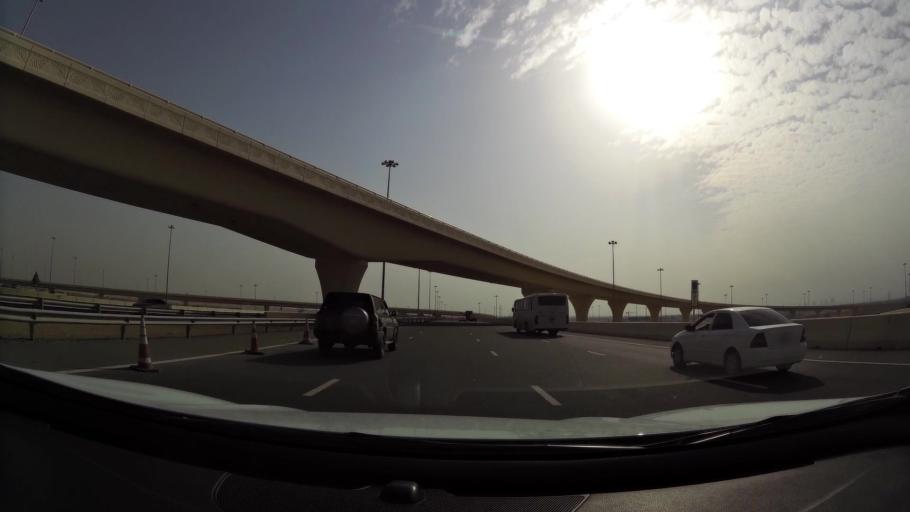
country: AE
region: Abu Dhabi
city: Abu Dhabi
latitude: 24.3114
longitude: 54.6027
